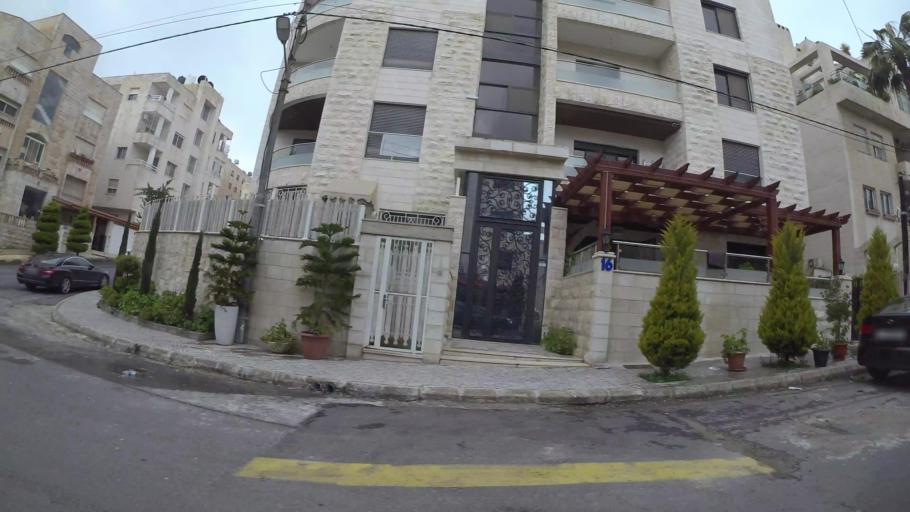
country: JO
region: Amman
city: Wadi as Sir
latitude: 31.9411
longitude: 35.8682
